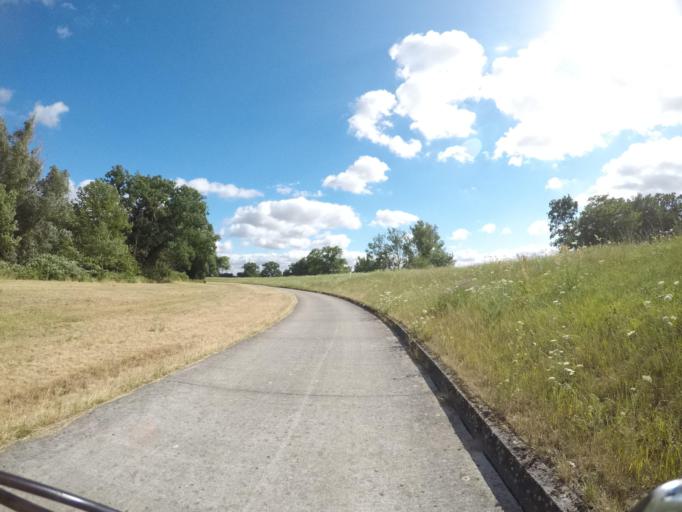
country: DE
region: Lower Saxony
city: Damnatz
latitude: 53.1681
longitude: 11.1653
